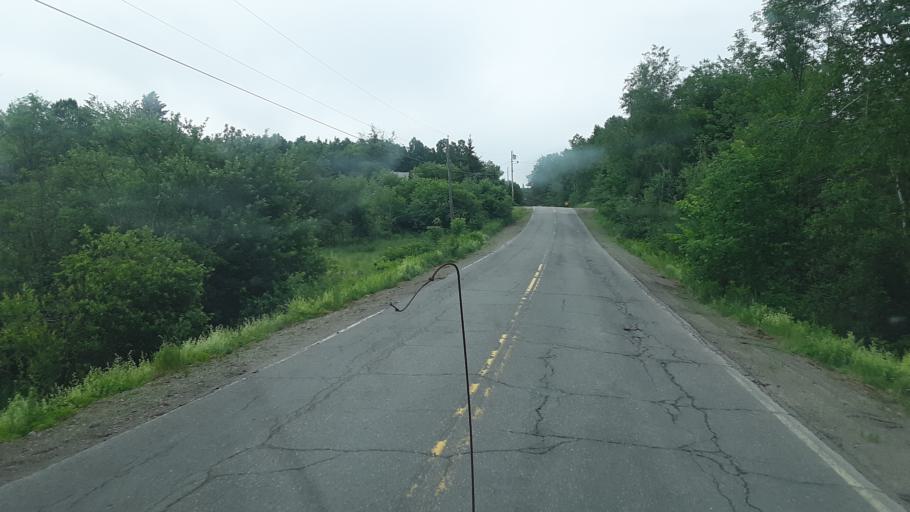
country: US
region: Maine
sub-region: Penobscot County
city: Orrington
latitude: 44.6991
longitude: -68.8692
